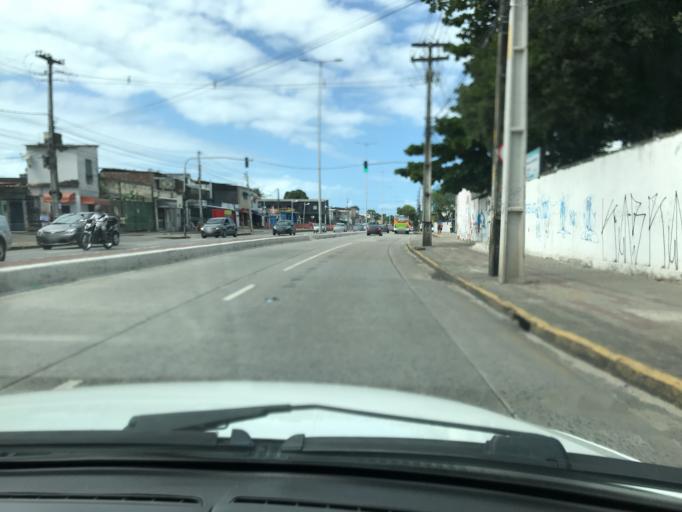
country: BR
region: Pernambuco
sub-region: Recife
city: Recife
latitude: -8.0446
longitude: -34.8810
